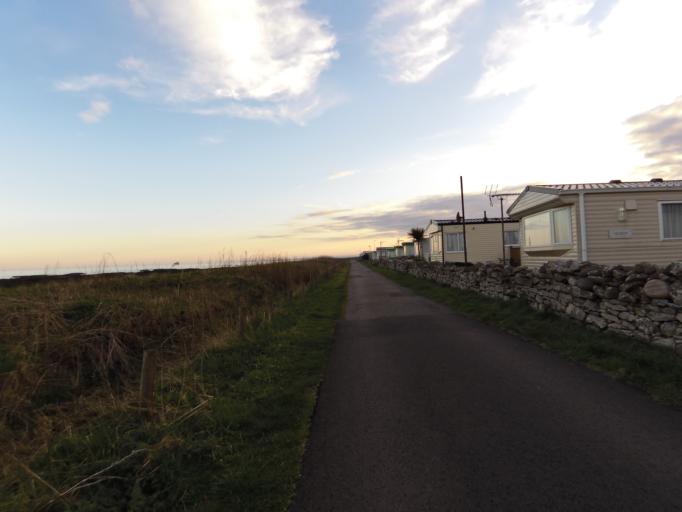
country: GB
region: Scotland
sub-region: Aberdeenshire
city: Inverbervie
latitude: 56.7976
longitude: -2.3240
